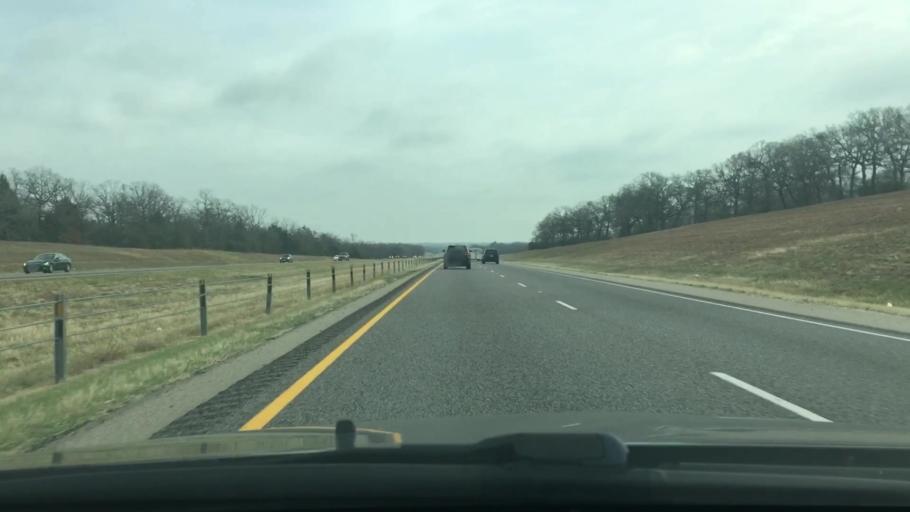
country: US
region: Texas
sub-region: Leon County
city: Buffalo
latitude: 31.5299
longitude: -96.1161
